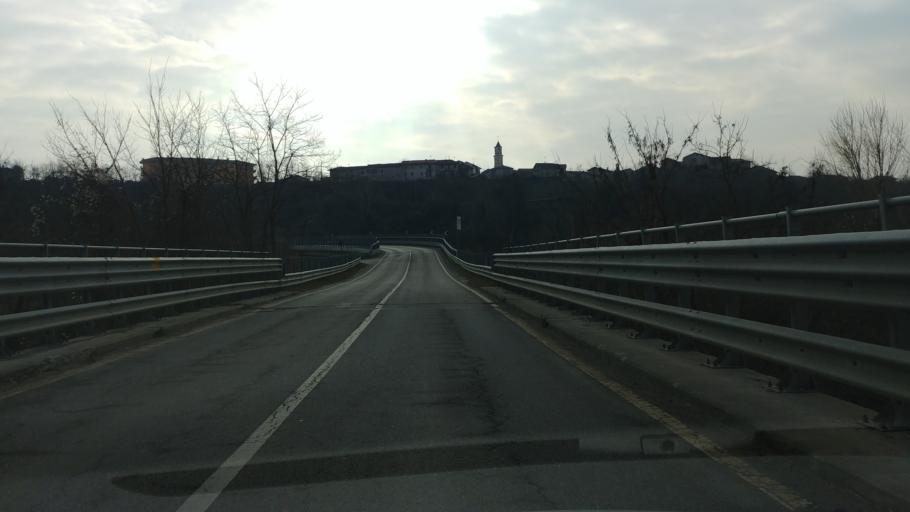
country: IT
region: Piedmont
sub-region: Provincia di Cuneo
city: Castelletto Stura
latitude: 44.4486
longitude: 7.6372
